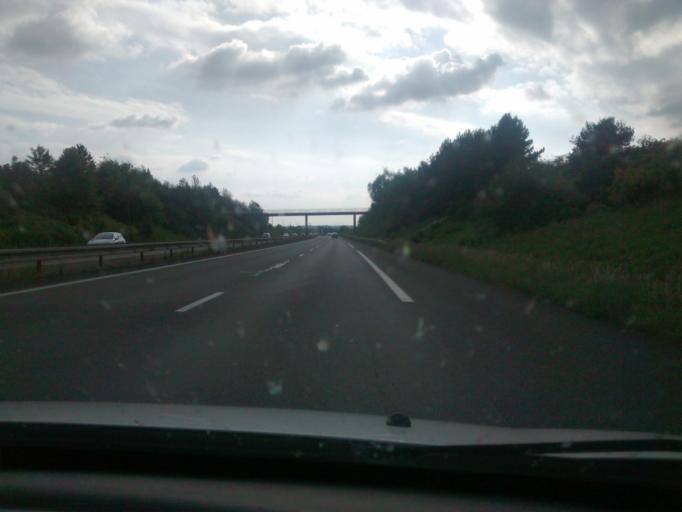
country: FR
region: Pays de la Loire
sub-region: Departement de la Mayenne
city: Argentre
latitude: 48.0753
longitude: -0.6192
